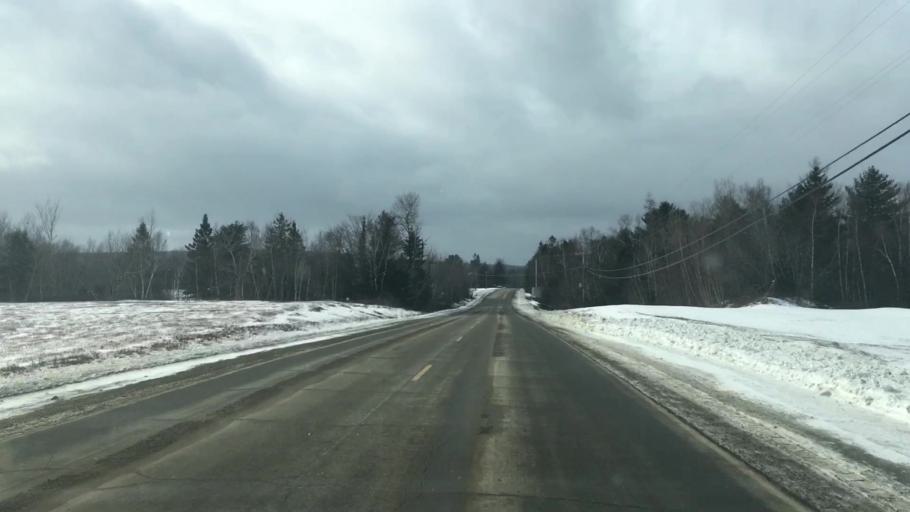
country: US
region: Maine
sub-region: Washington County
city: Calais
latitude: 45.0208
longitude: -67.3806
